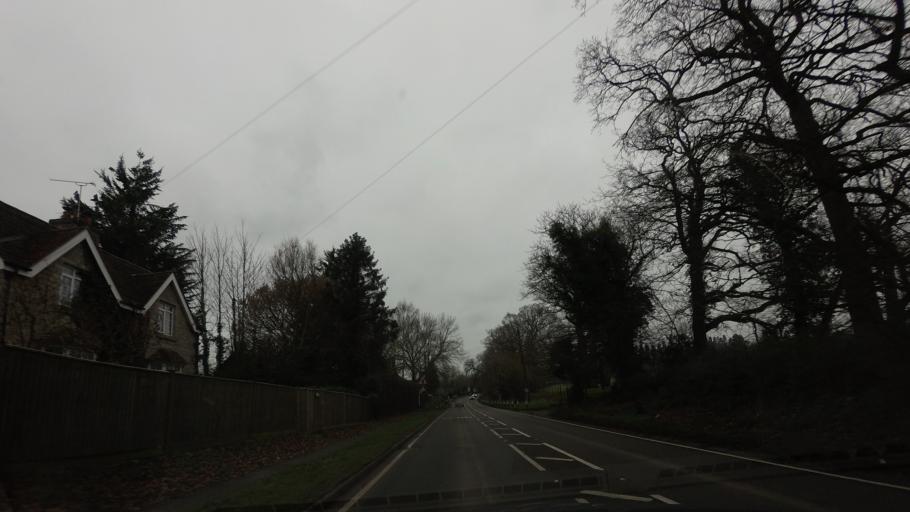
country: GB
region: England
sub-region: Kent
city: Marden
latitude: 51.2167
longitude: 0.5118
